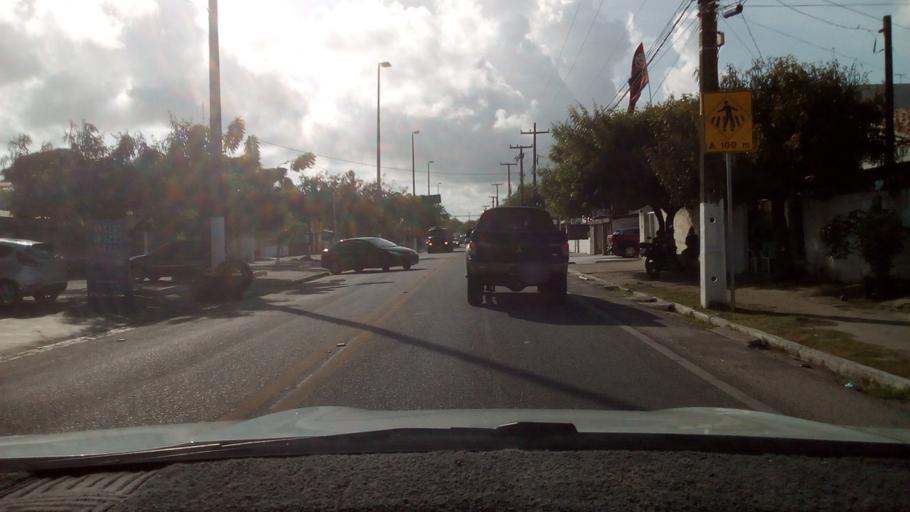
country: BR
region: Paraiba
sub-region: Cabedelo
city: Cabedelo
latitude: -6.9718
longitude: -34.8349
